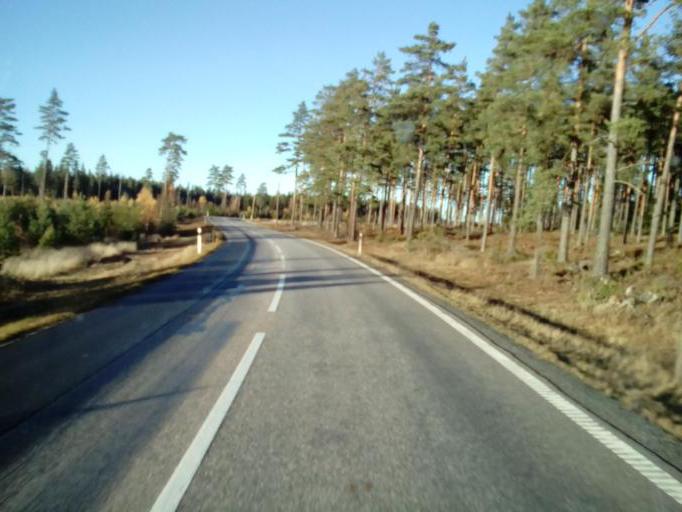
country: SE
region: OErebro
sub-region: Hallsbergs Kommun
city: Palsboda
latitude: 58.8512
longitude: 15.4048
